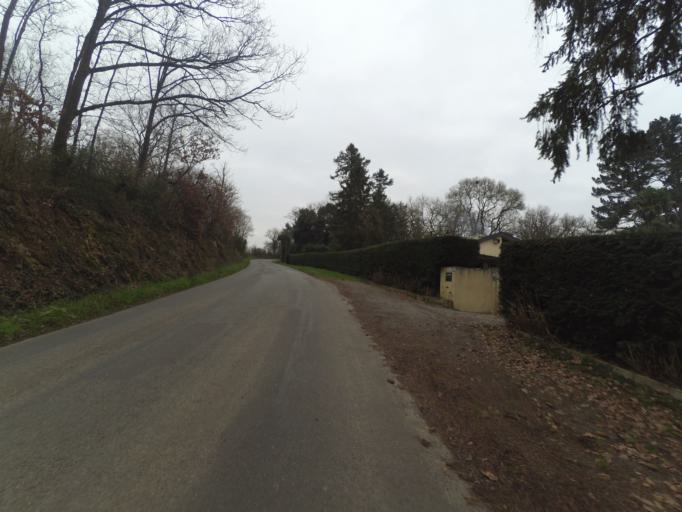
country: FR
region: Pays de la Loire
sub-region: Departement de la Loire-Atlantique
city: Coueron
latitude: 47.2325
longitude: -1.6935
